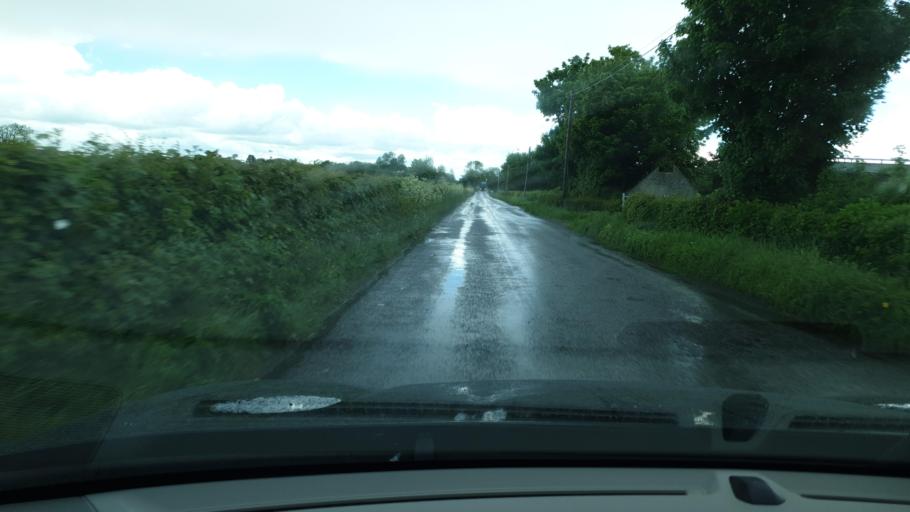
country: IE
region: Leinster
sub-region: Laois
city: Mountmellick
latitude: 53.1325
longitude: -7.3738
